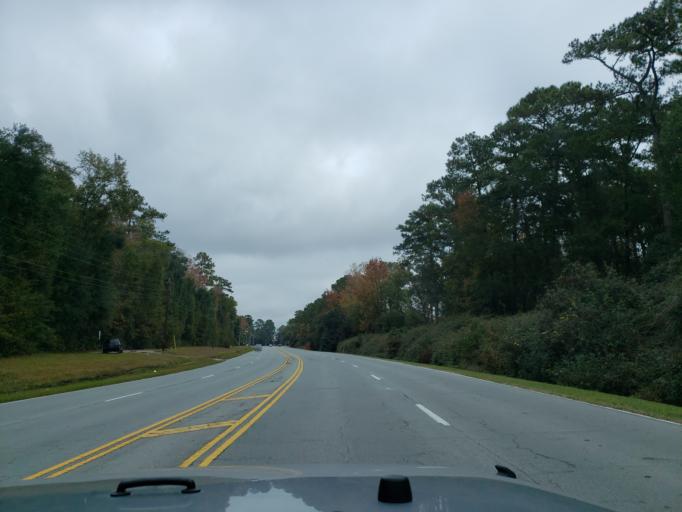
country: US
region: Georgia
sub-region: Chatham County
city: Whitemarsh Island
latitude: 32.0321
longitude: -80.9930
